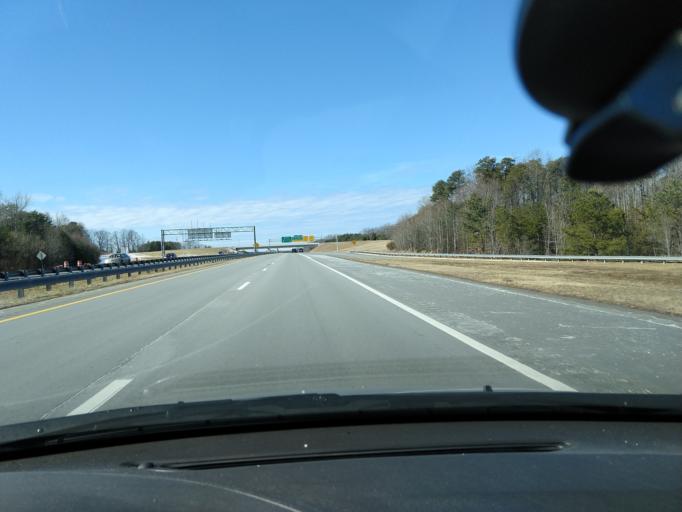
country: US
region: North Carolina
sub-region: Guilford County
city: Summerfield
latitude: 36.1182
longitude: -79.9116
